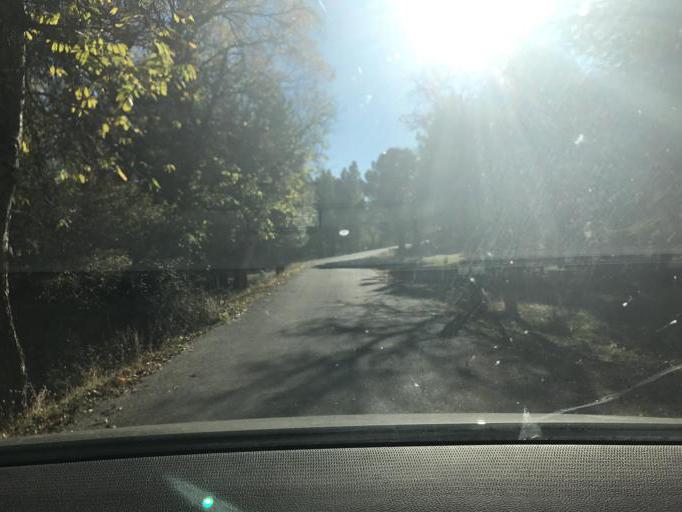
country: ES
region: Andalusia
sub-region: Provincia de Granada
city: Beas de Granada
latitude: 37.3060
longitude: -3.4645
